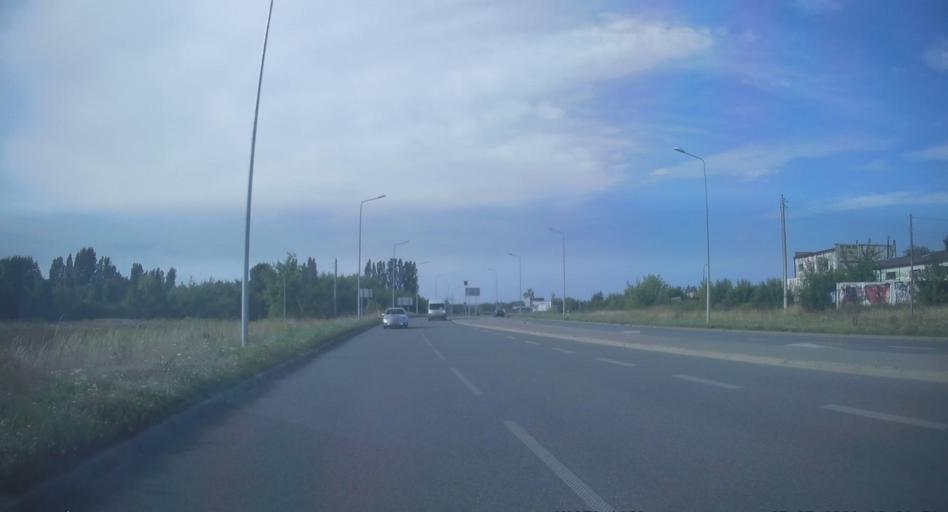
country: PL
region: Swietokrzyskie
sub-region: Powiat konecki
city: Konskie
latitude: 51.2006
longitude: 20.3998
